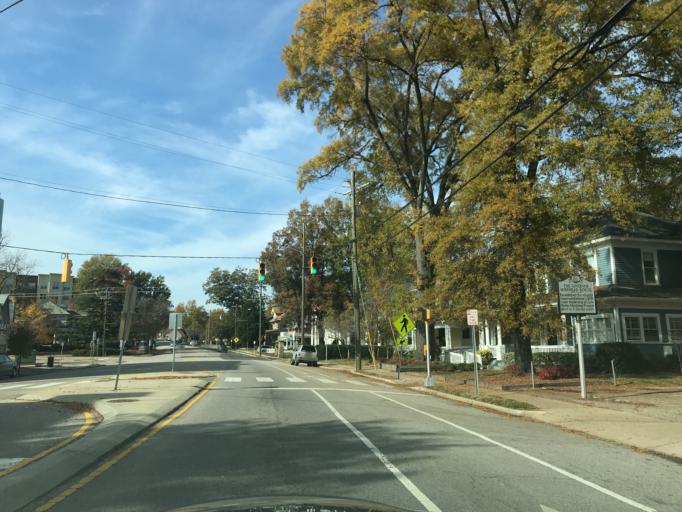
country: US
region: North Carolina
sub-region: Wake County
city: West Raleigh
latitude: 35.7831
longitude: -78.6557
